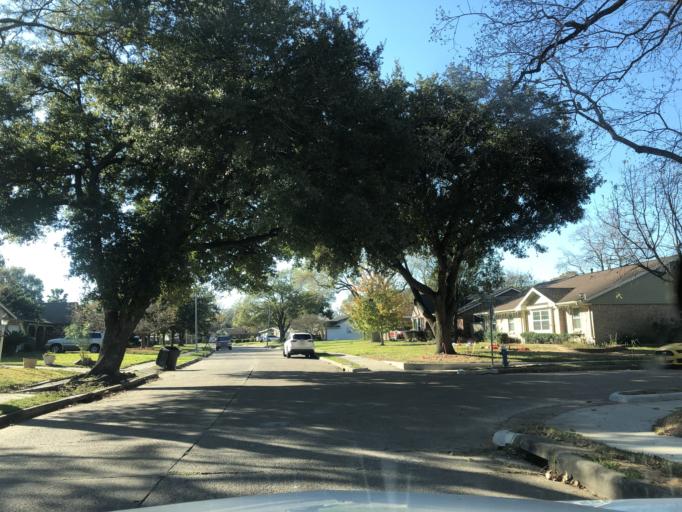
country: US
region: Texas
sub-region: Harris County
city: Bellaire
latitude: 29.6948
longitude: -95.5084
